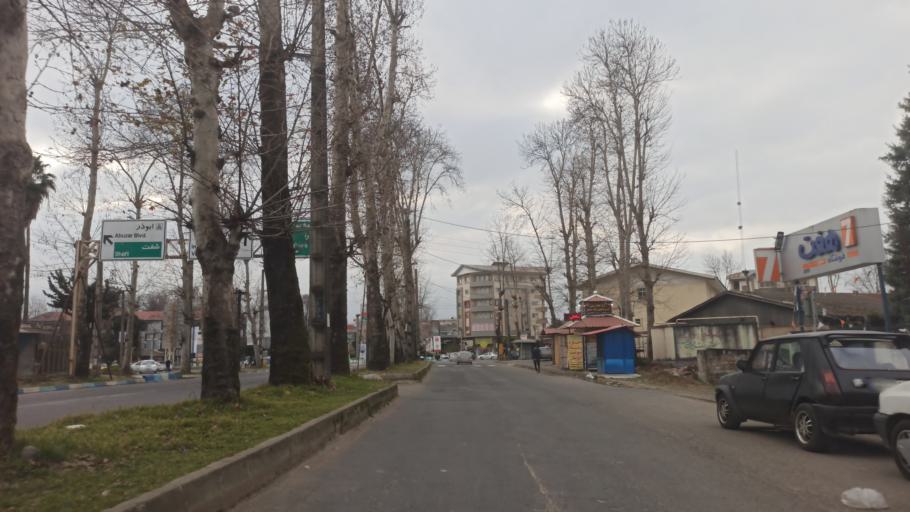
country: IR
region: Gilan
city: Fuman
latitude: 37.2335
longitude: 49.3201
